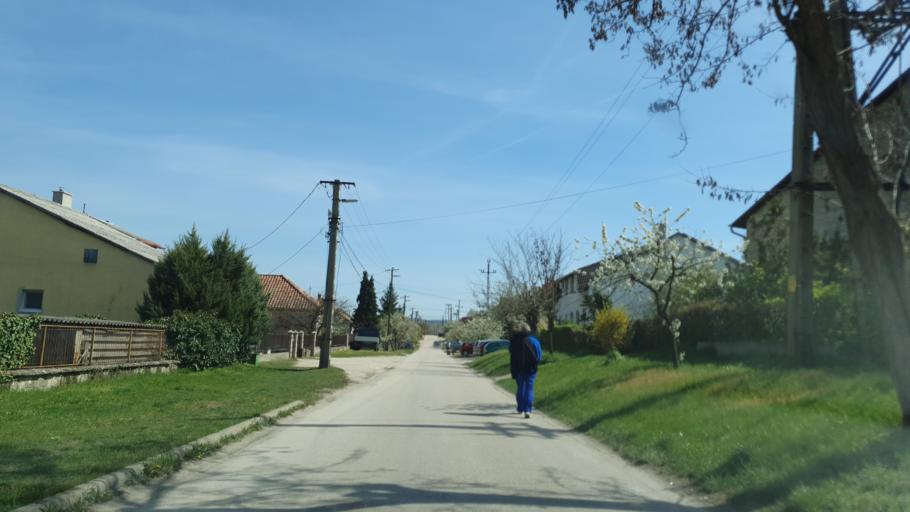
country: HU
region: Komarom-Esztergom
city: Oroszlany
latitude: 47.4902
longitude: 18.3029
